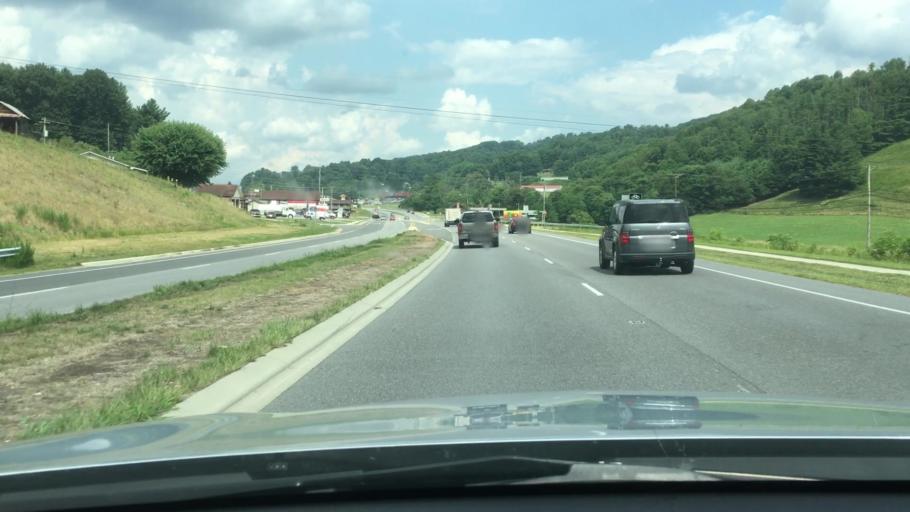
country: US
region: North Carolina
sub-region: Yancey County
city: Burnsville
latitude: 35.9125
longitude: -82.3196
